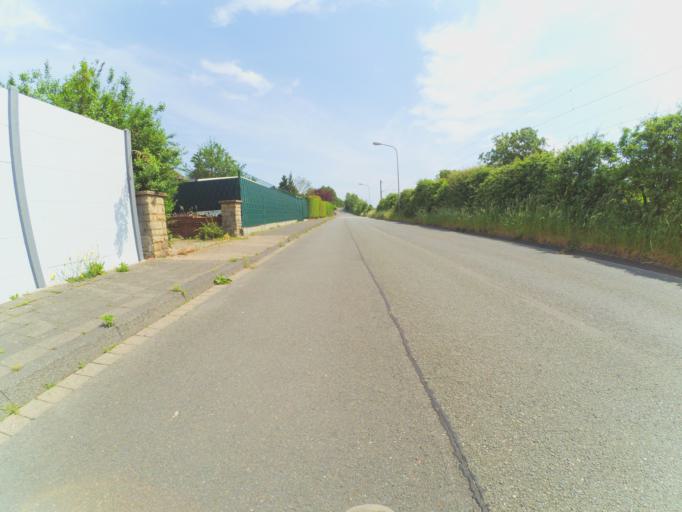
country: DE
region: North Rhine-Westphalia
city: Ibbenburen
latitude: 52.2842
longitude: 7.7087
